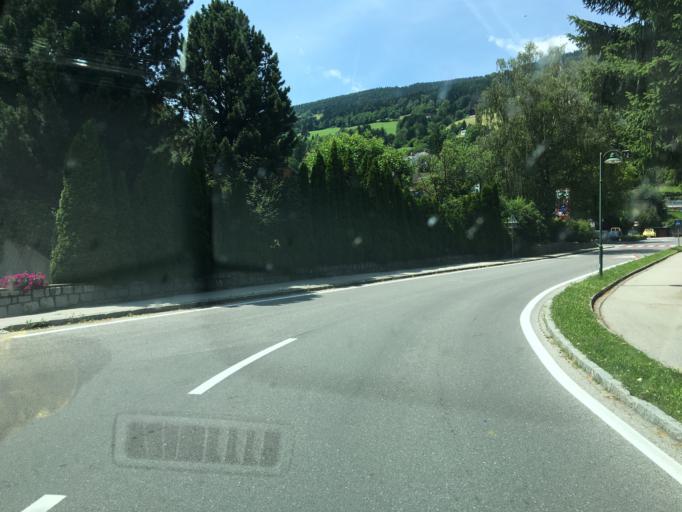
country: AT
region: Carinthia
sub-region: Politischer Bezirk Spittal an der Drau
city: Winklern
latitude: 46.8696
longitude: 12.8781
